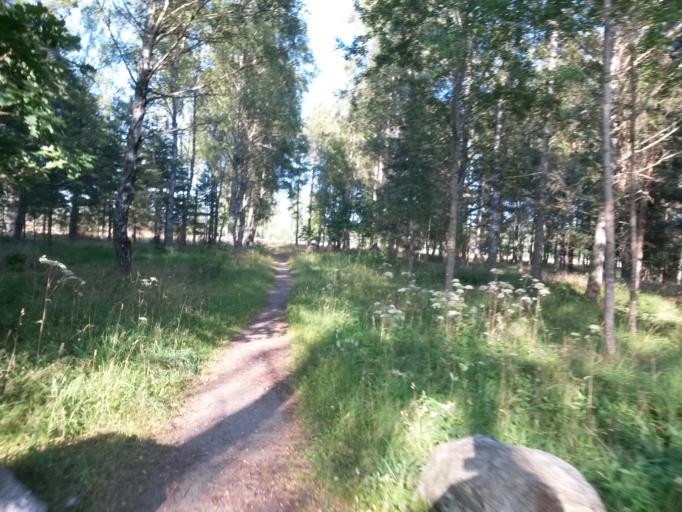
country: SE
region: Vaestra Goetaland
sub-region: Vargarda Kommun
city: Vargarda
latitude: 58.0263
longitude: 12.8191
